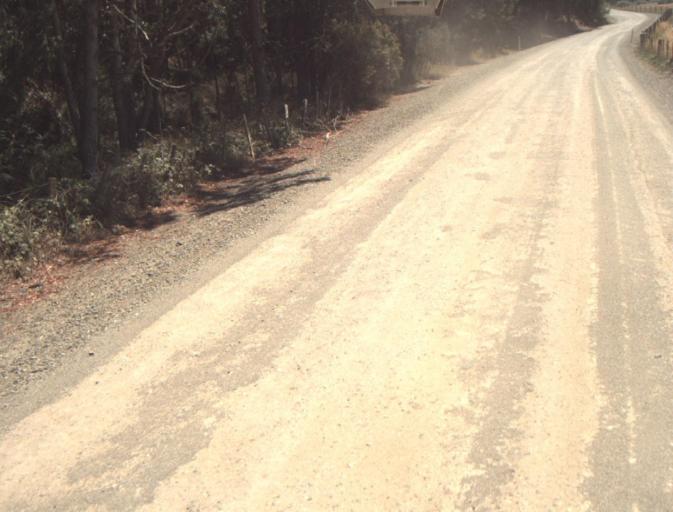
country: AU
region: Tasmania
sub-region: Dorset
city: Scottsdale
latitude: -41.2897
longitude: 147.3919
